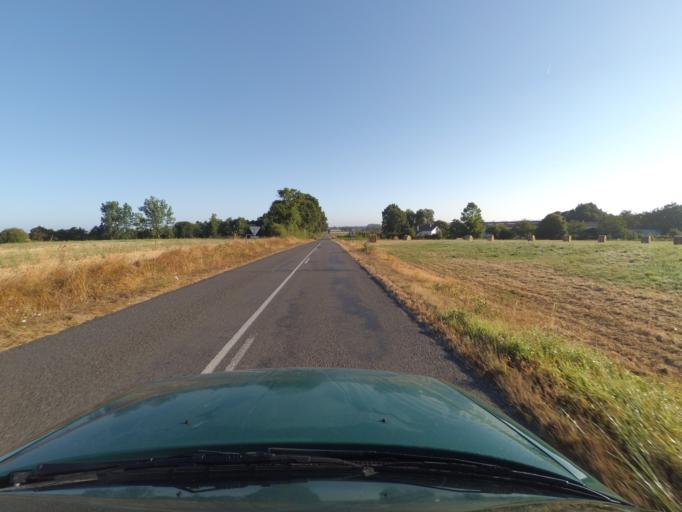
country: FR
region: Pays de la Loire
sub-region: Departement de la Loire-Atlantique
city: La Planche
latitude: 46.9977
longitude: -1.4554
